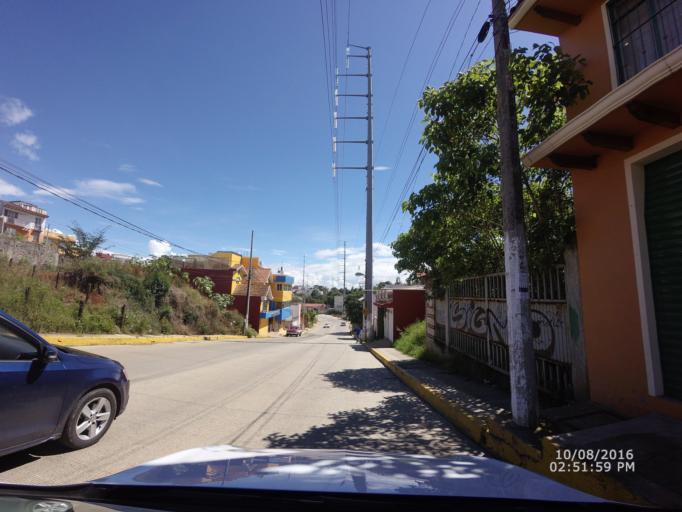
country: MX
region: Veracruz
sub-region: Xalapa
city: Colonia Santa Barbara
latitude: 19.5056
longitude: -96.8789
